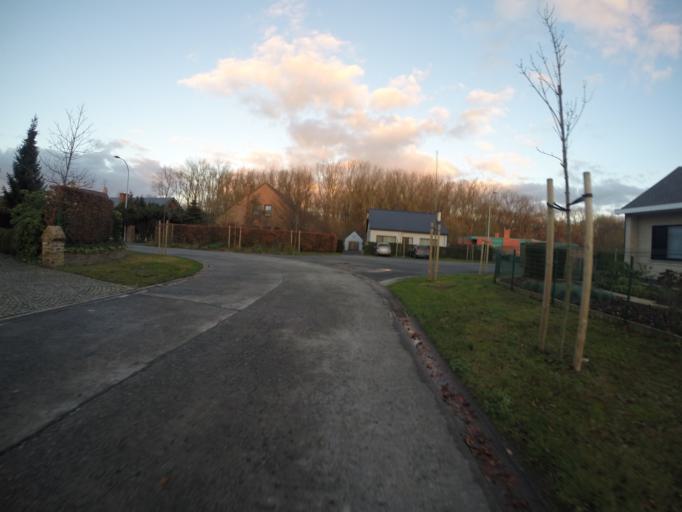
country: BE
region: Flanders
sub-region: Provincie Oost-Vlaanderen
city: Aalter
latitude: 51.0924
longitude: 3.4634
